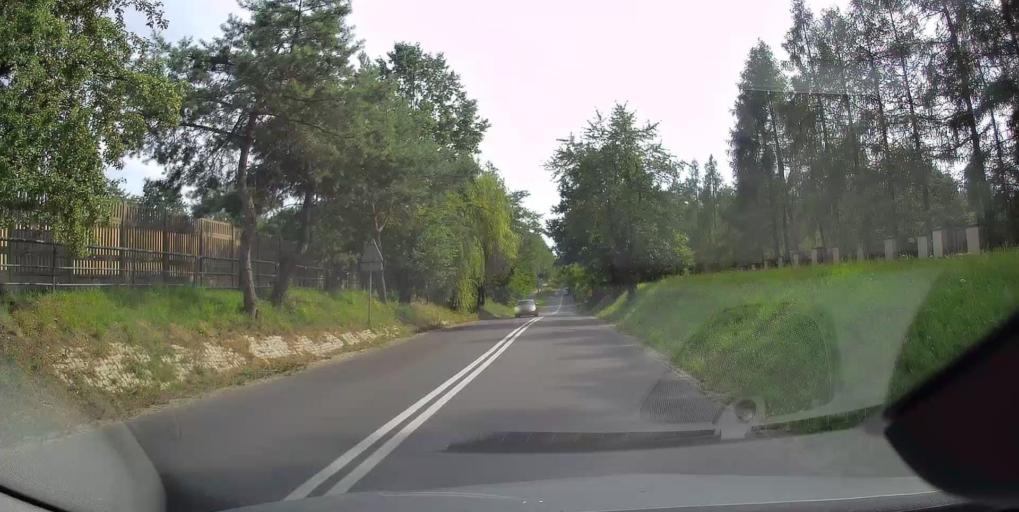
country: PL
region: Lodz Voivodeship
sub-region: Powiat tomaszowski
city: Tomaszow Mazowiecki
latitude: 51.5167
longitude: 20.0016
